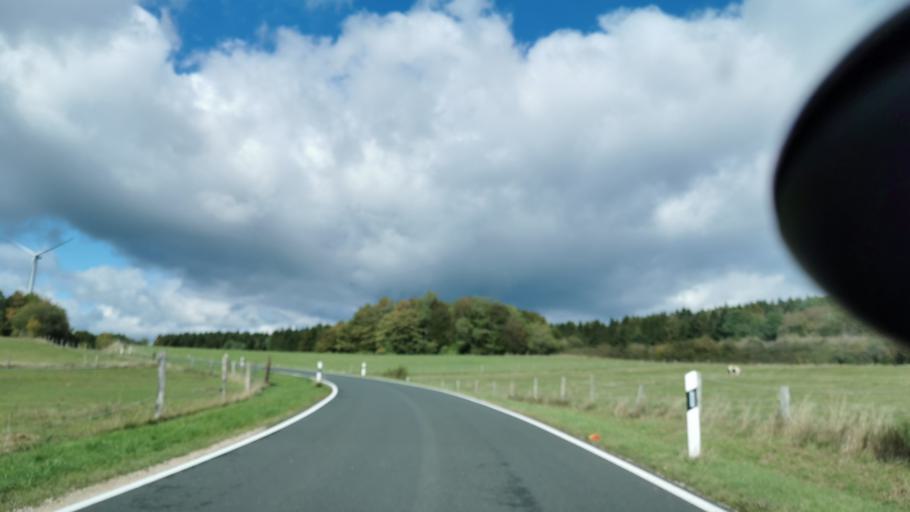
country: DE
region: Rheinland-Pfalz
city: Betteldorf
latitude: 50.2628
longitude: 6.7472
